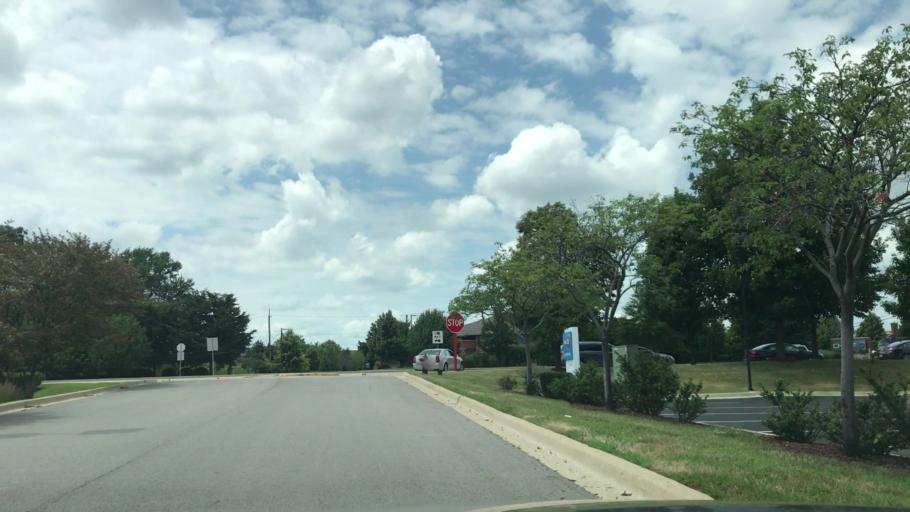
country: US
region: Illinois
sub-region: DuPage County
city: Warrenville
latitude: 41.7808
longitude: -88.2400
